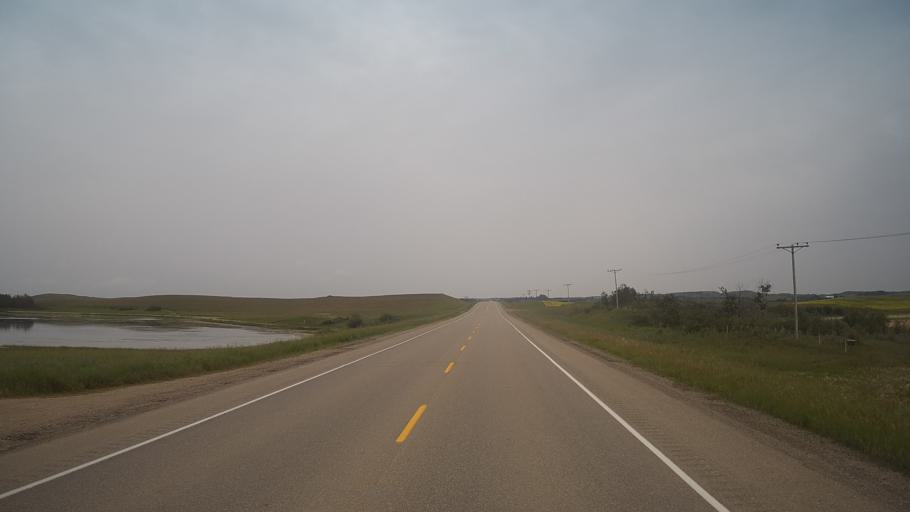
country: CA
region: Saskatchewan
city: Biggar
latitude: 52.0565
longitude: -107.8207
